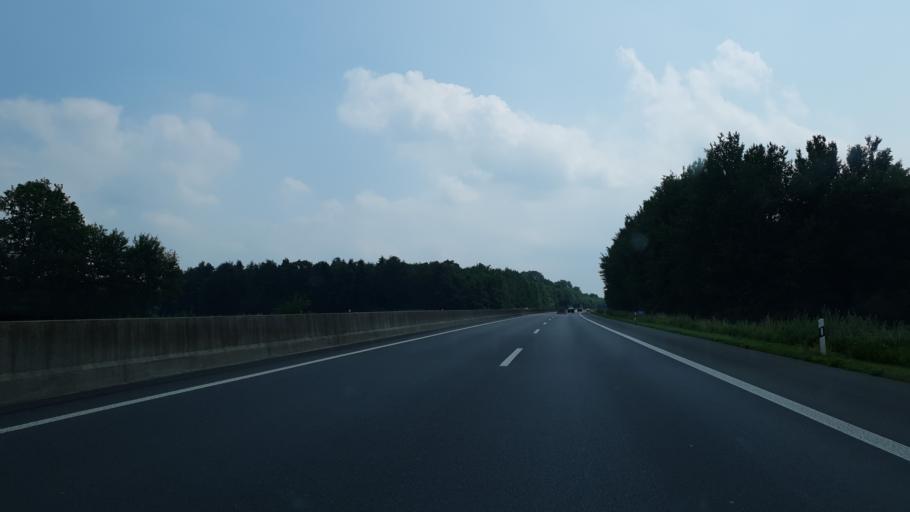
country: DE
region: North Rhine-Westphalia
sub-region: Regierungsbezirk Munster
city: Gescher
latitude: 51.9849
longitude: 7.0499
